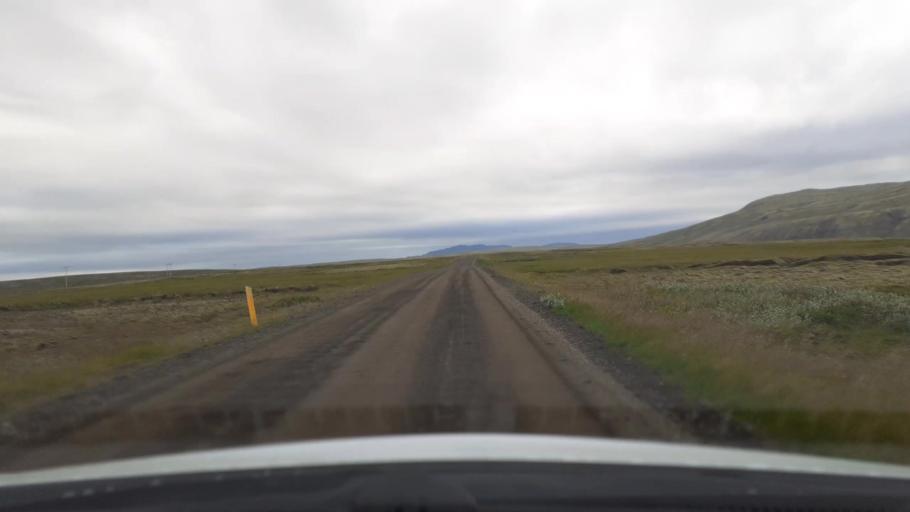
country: IS
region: Capital Region
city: Mosfellsbaer
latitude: 64.1958
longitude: -21.5480
